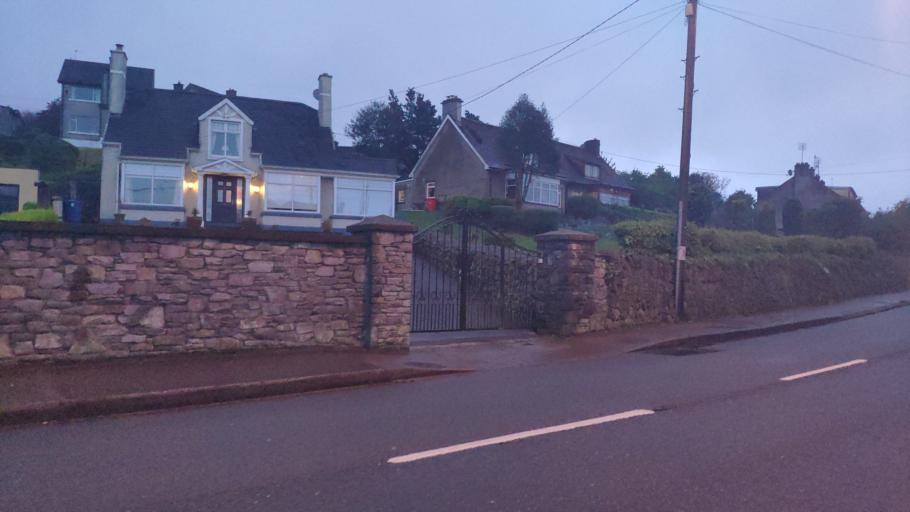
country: IE
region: Munster
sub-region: County Cork
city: Cork
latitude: 51.9108
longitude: -8.4534
